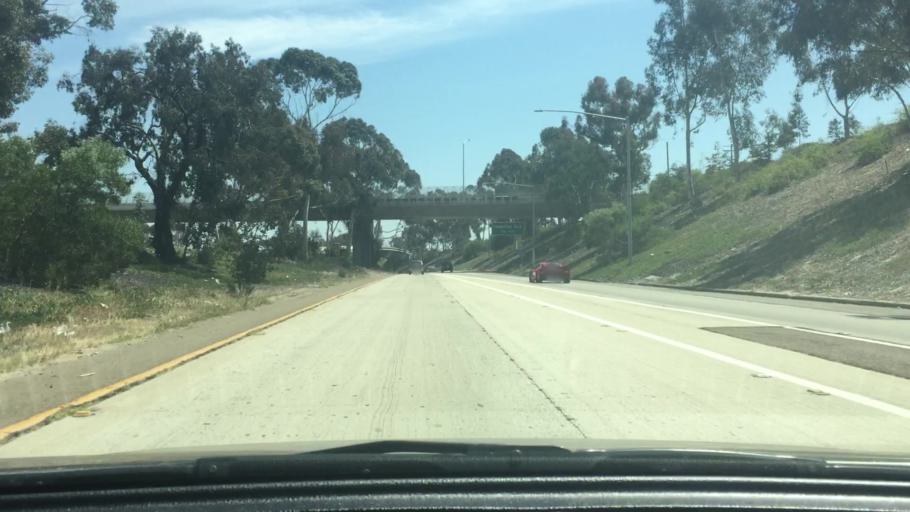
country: US
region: California
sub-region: San Diego County
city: National City
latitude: 32.7164
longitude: -117.1038
